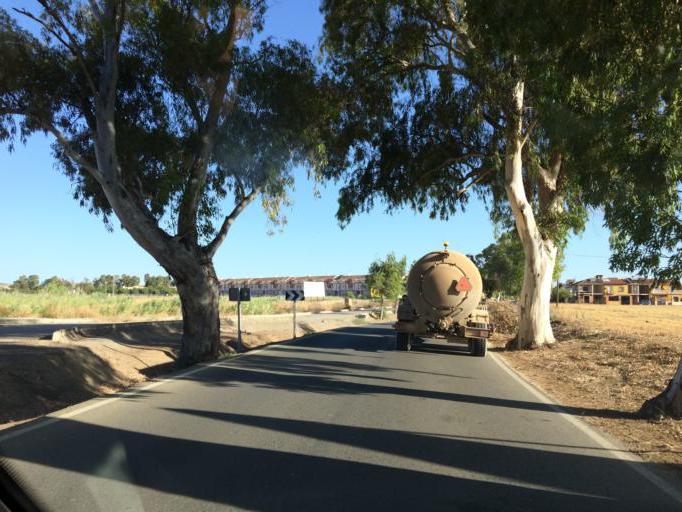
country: ES
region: Andalusia
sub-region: Provincia de Malaga
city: Campillos
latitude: 37.0393
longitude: -4.8587
